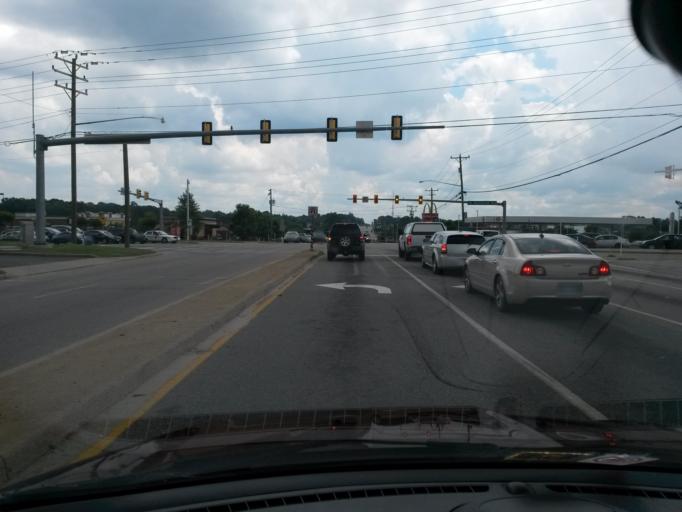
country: US
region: Virginia
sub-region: Chesterfield County
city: Chester
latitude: 37.3554
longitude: -77.4133
